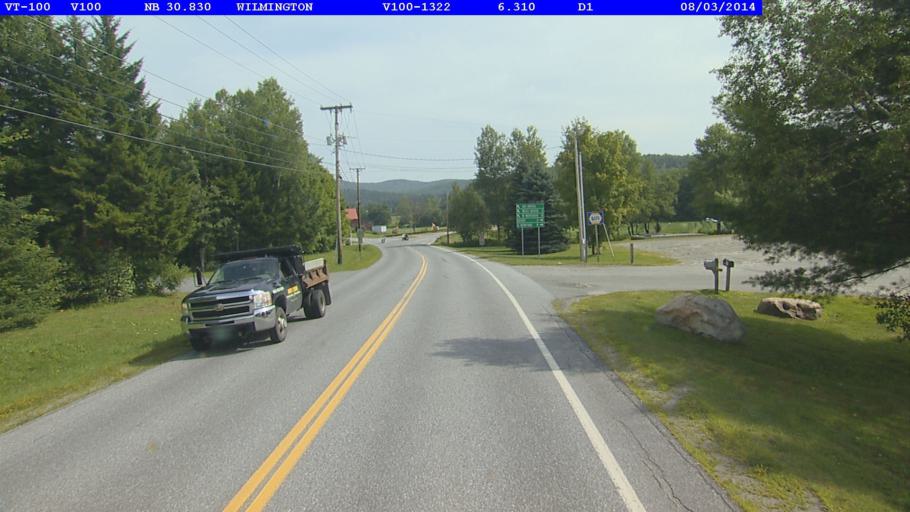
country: US
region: Vermont
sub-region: Windham County
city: Dover
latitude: 42.9123
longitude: -72.8399
